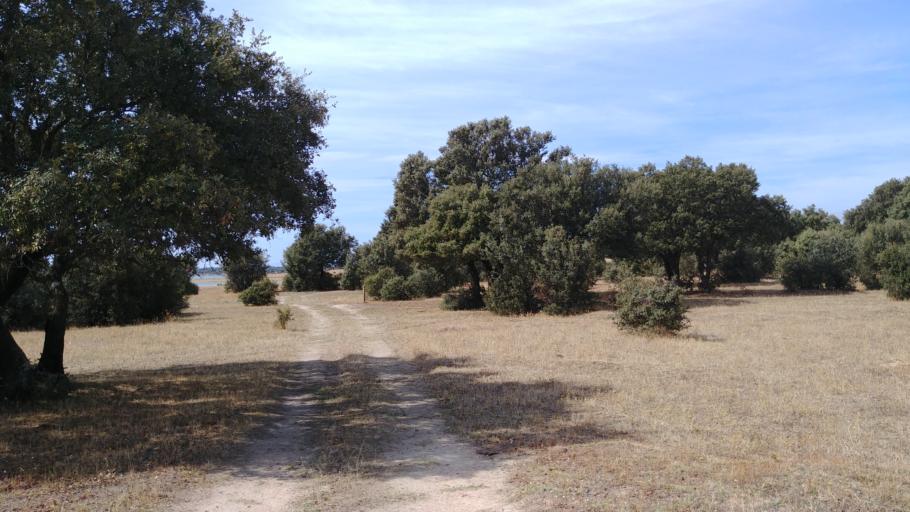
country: ES
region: Castille-La Mancha
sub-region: Province of Toledo
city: Navalcan
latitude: 40.0468
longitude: -5.1169
